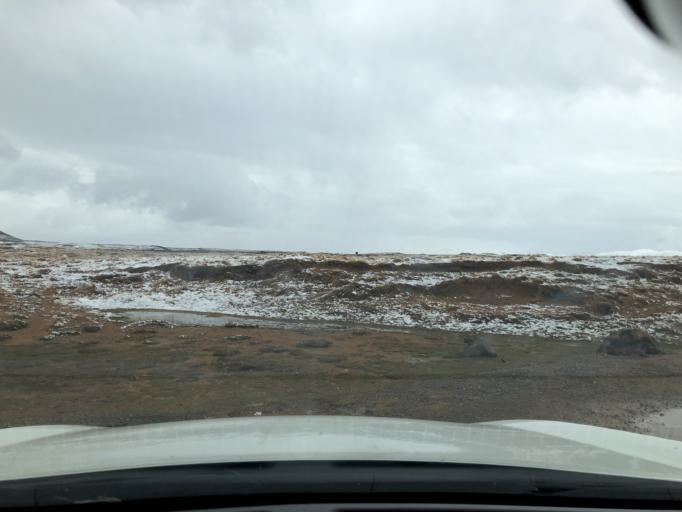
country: IS
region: Northeast
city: Laugar
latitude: 65.6417
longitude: -16.8066
